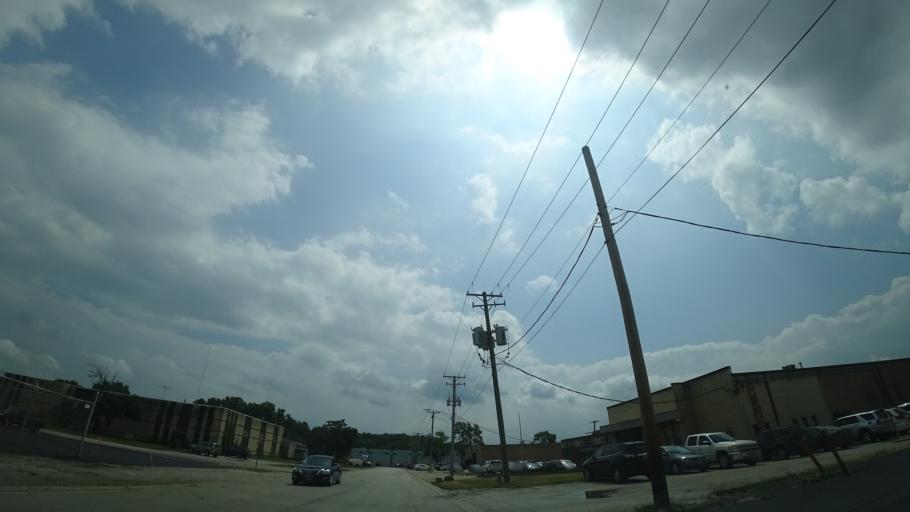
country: US
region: Illinois
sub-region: Cook County
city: Crestwood
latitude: 41.6791
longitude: -87.7662
